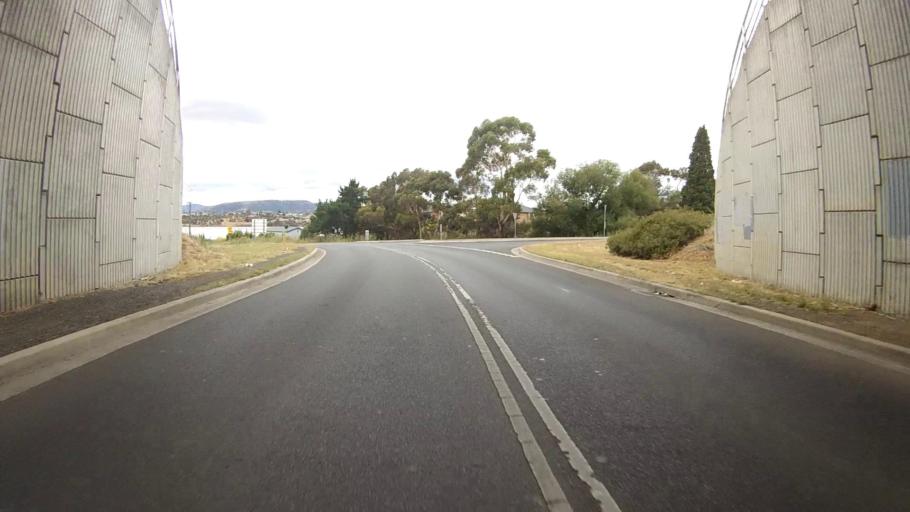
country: AU
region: Tasmania
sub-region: Glenorchy
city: Granton
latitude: -42.7524
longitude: 147.2286
